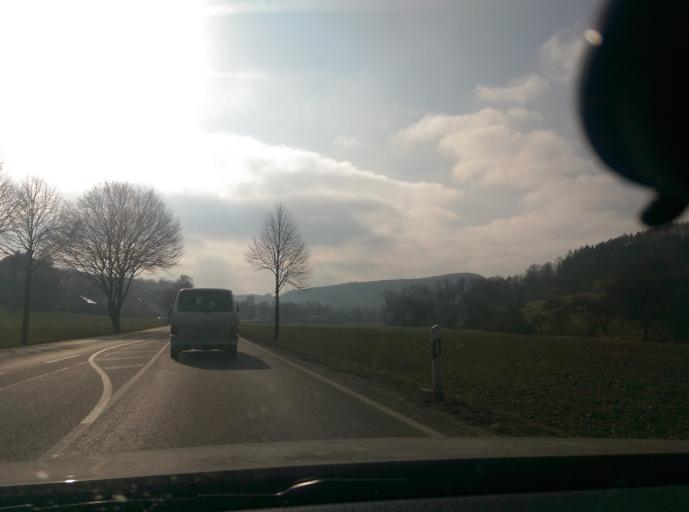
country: DE
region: Hesse
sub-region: Regierungsbezirk Kassel
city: Sontra
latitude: 51.0515
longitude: 10.0080
